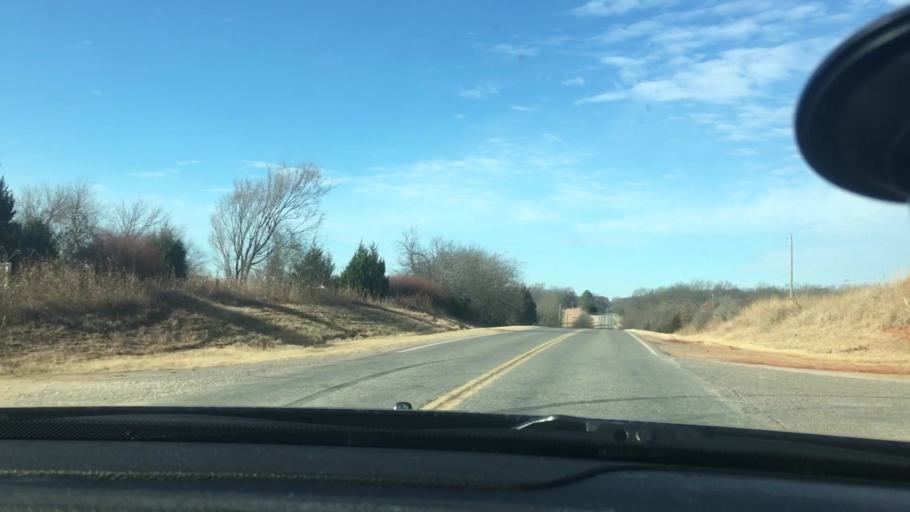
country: US
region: Oklahoma
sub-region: Seminole County
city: Konawa
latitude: 34.9856
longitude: -96.8092
